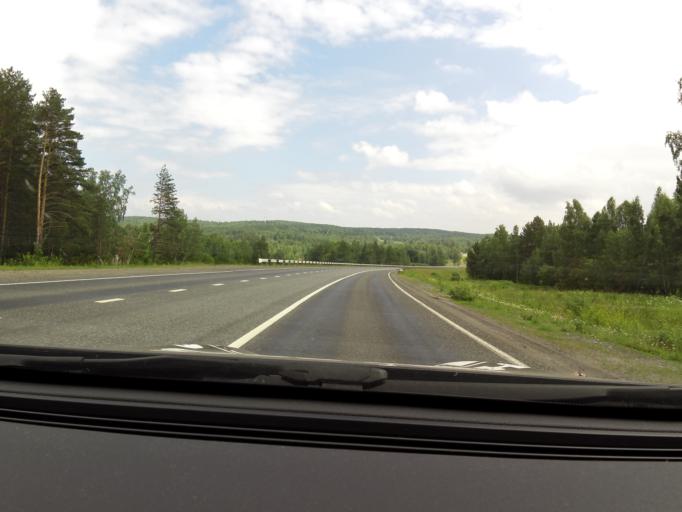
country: RU
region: Perm
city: Suksun
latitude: 57.0948
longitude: 57.3512
